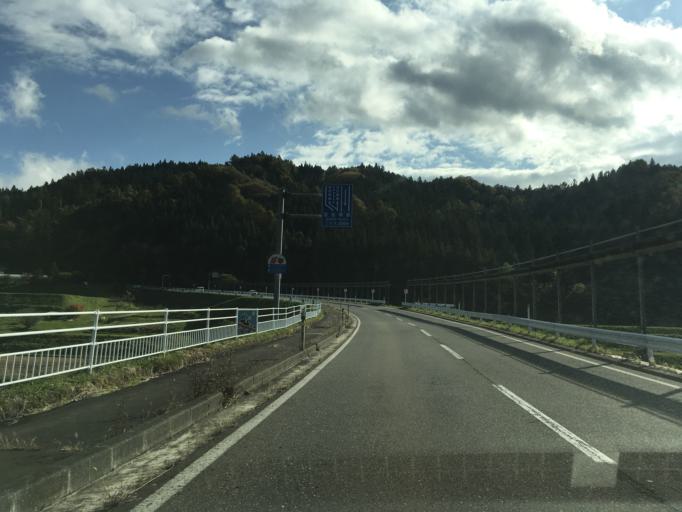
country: JP
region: Iwate
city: Tono
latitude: 39.3648
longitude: 141.4009
